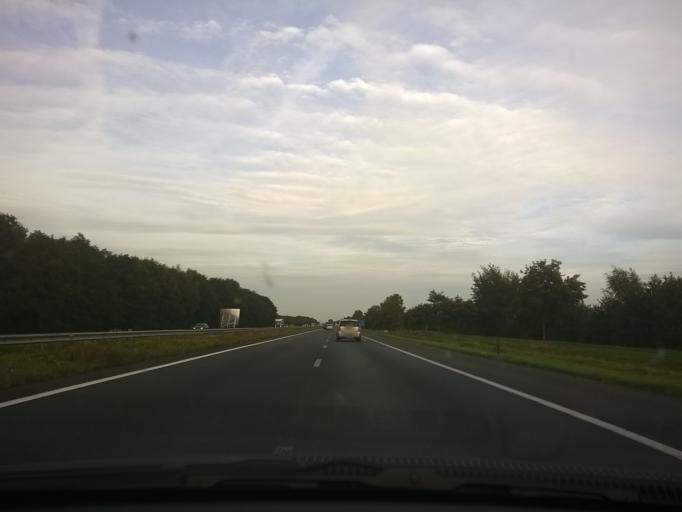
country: NL
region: Friesland
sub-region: Gemeente Achtkarspelen
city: Surhuisterveen
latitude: 53.1346
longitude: 6.2013
